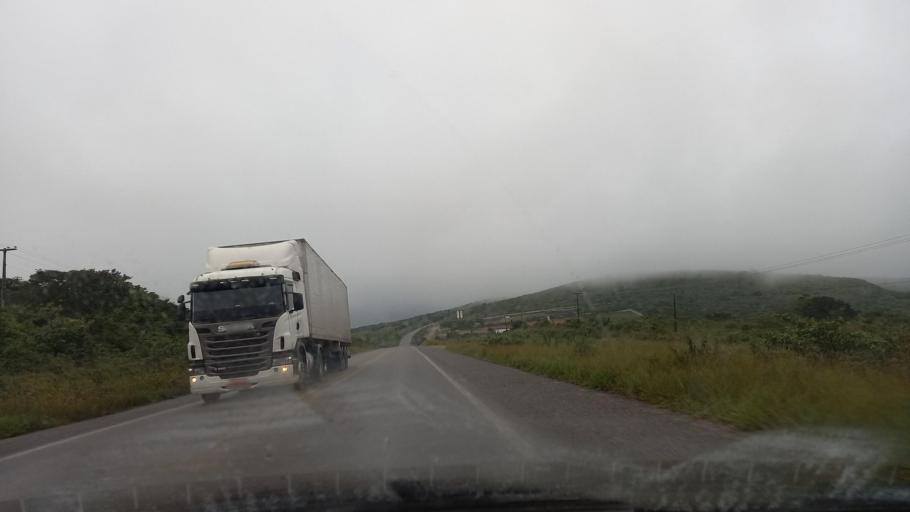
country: BR
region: Pernambuco
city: Garanhuns
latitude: -8.8747
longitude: -36.5298
